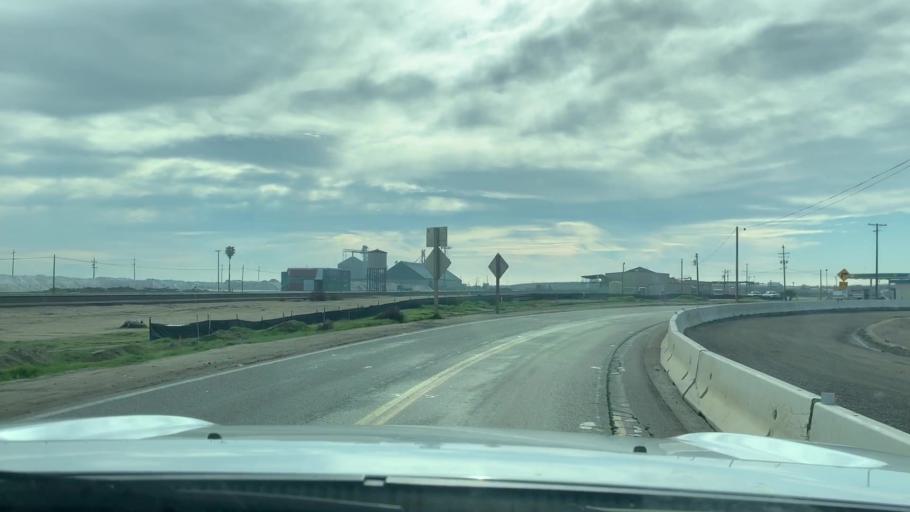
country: US
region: California
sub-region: Kern County
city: McFarland
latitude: 35.6013
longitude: -119.2093
